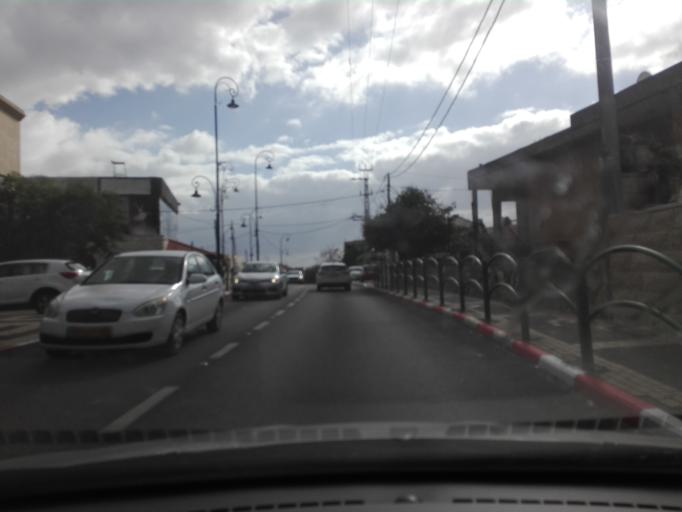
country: IL
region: Haifa
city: Daliyat el Karmil
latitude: 32.7202
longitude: 35.0624
